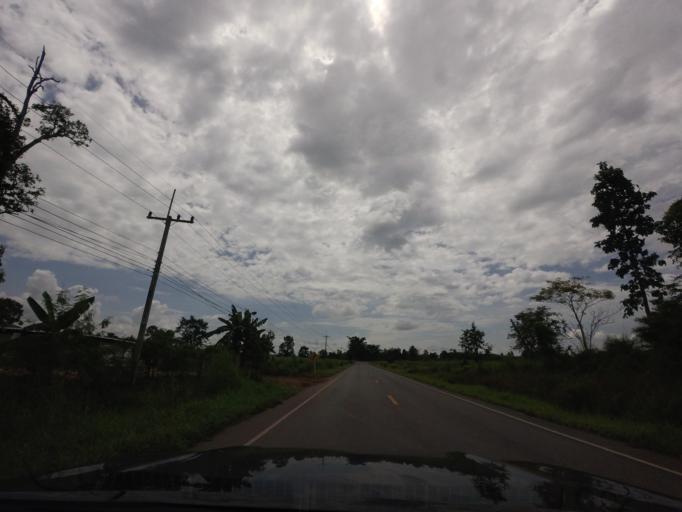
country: TH
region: Changwat Udon Thani
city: Nam Som
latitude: 17.8220
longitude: 102.2707
